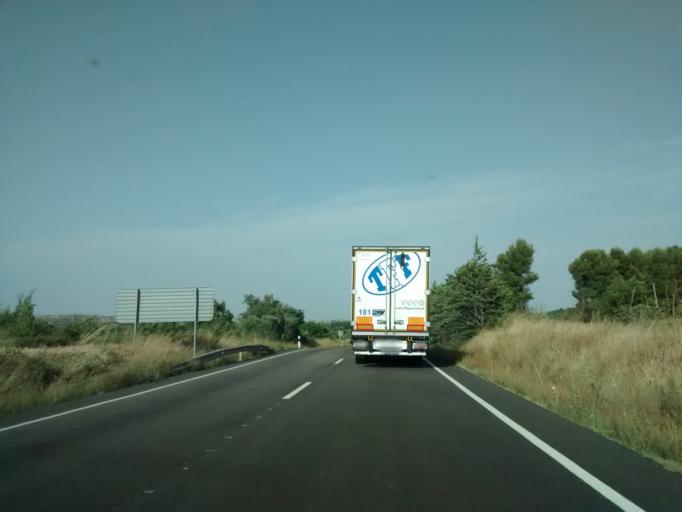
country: ES
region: Aragon
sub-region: Provincia de Zaragoza
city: Bulbuente
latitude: 41.8209
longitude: -1.5979
